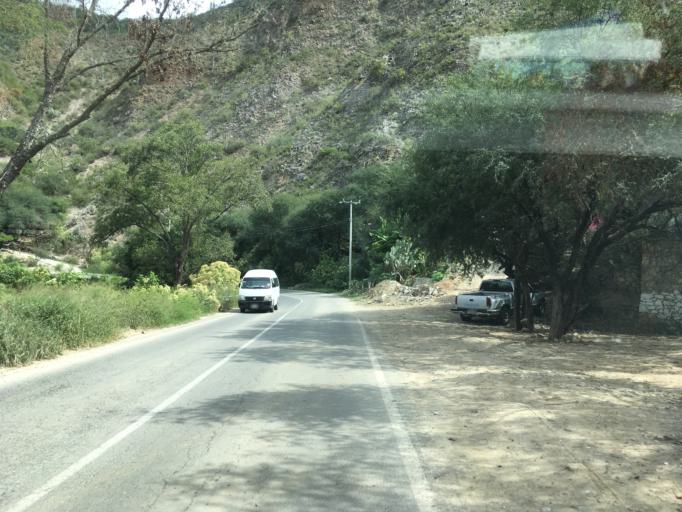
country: MX
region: Hidalgo
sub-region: San Agustin Metzquititlan
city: Mezquititlan
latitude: 20.5308
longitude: -98.7187
